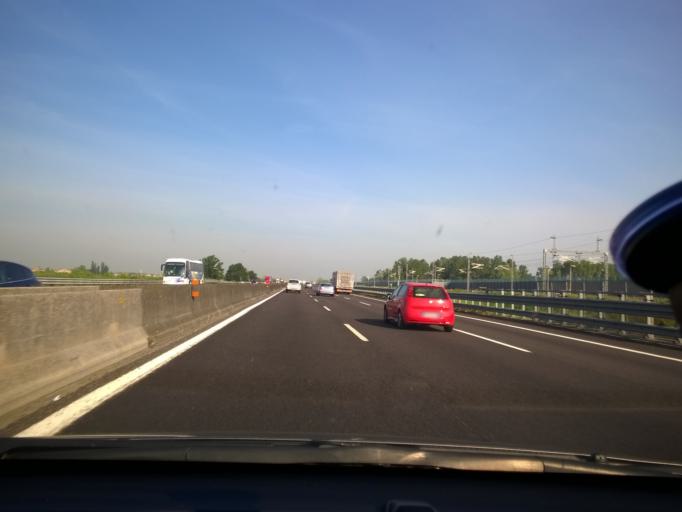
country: IT
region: Emilia-Romagna
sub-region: Provincia di Reggio Emilia
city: Campegine
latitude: 44.7601
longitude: 10.5366
